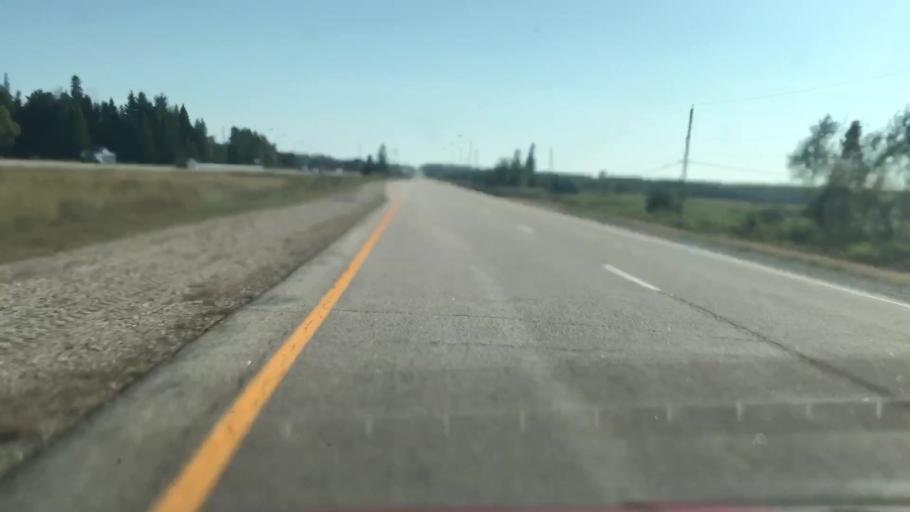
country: CA
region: Ontario
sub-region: Algoma
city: Sault Ste. Marie
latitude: 46.3713
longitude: -84.0680
